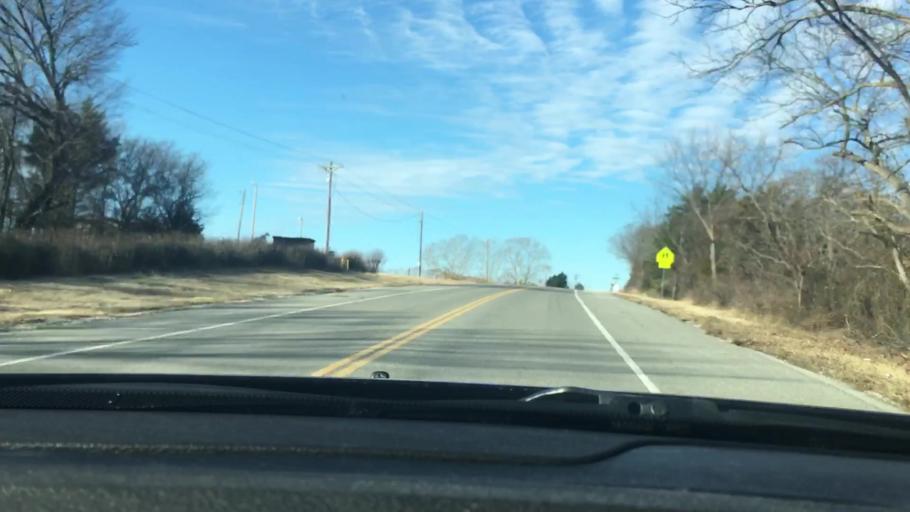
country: US
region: Oklahoma
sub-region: Love County
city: Marietta
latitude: 33.9402
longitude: -97.3141
